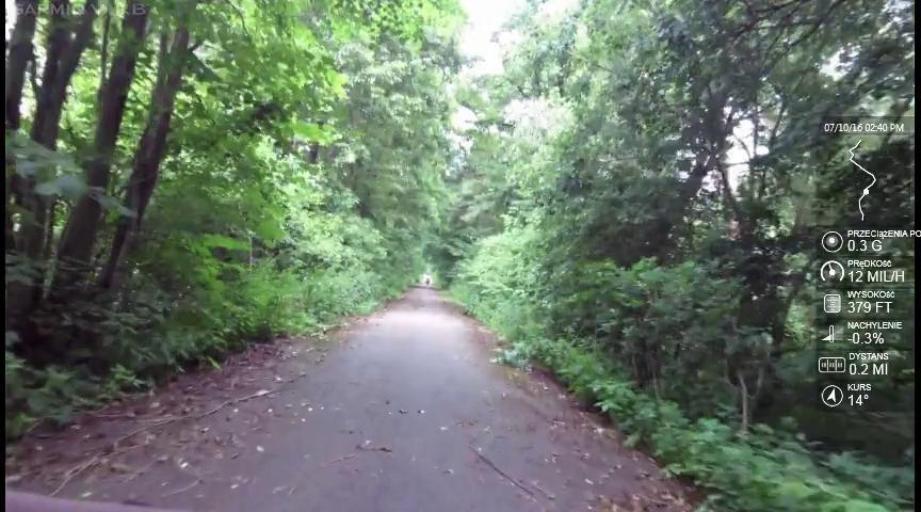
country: PL
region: West Pomeranian Voivodeship
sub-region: Powiat gryfinski
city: Banie
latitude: 53.0793
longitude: 14.6368
